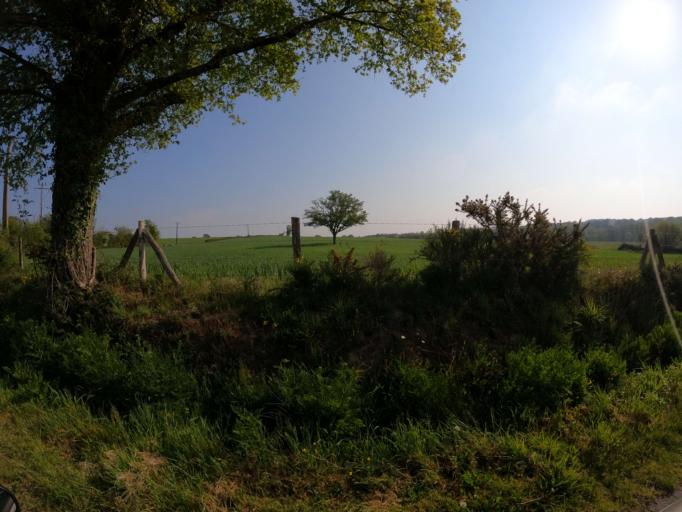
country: FR
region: Pays de la Loire
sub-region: Departement de Maine-et-Loire
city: La Seguiniere
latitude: 47.0700
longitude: -0.9633
